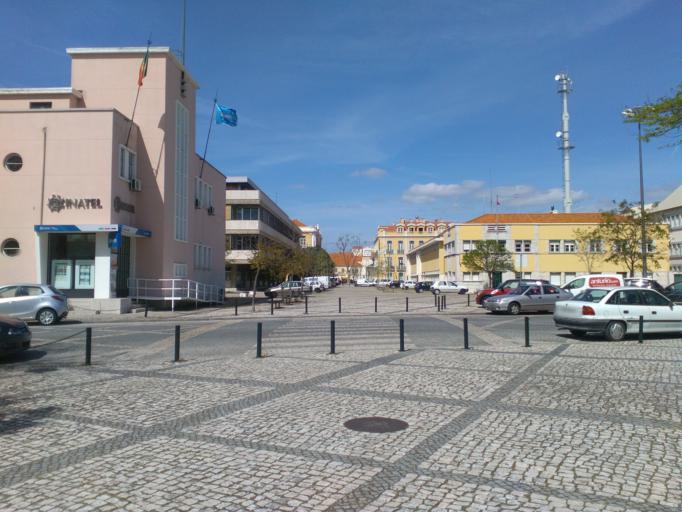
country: PT
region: Setubal
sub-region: Setubal
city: Setubal
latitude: 38.5211
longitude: -8.8915
